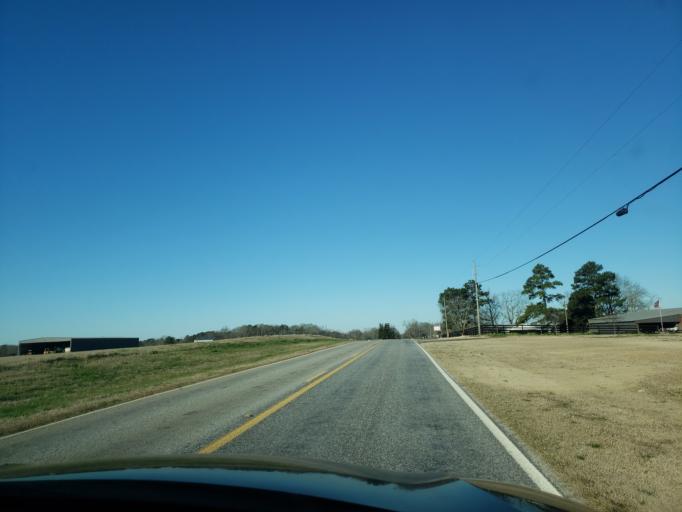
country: US
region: Alabama
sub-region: Elmore County
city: Tallassee
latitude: 32.5813
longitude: -85.7796
